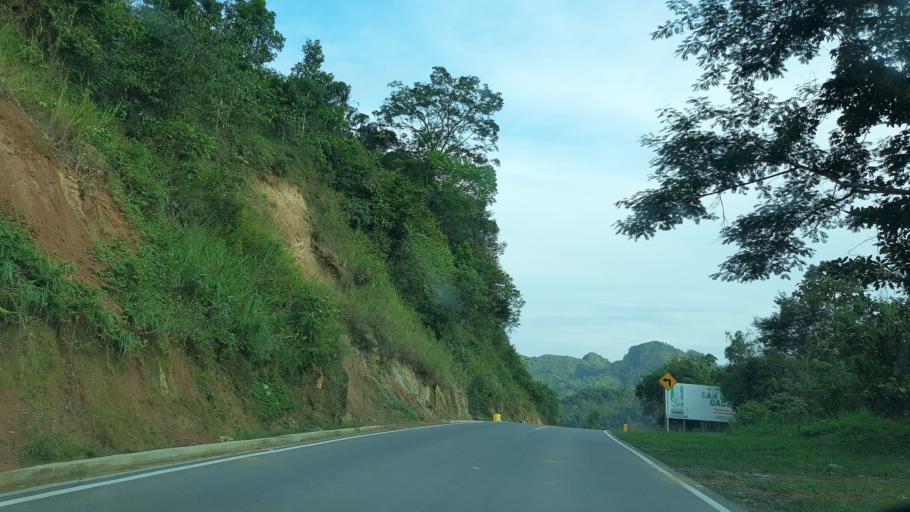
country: CO
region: Boyaca
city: San Luis de Gaceno
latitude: 4.8193
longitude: -73.1904
